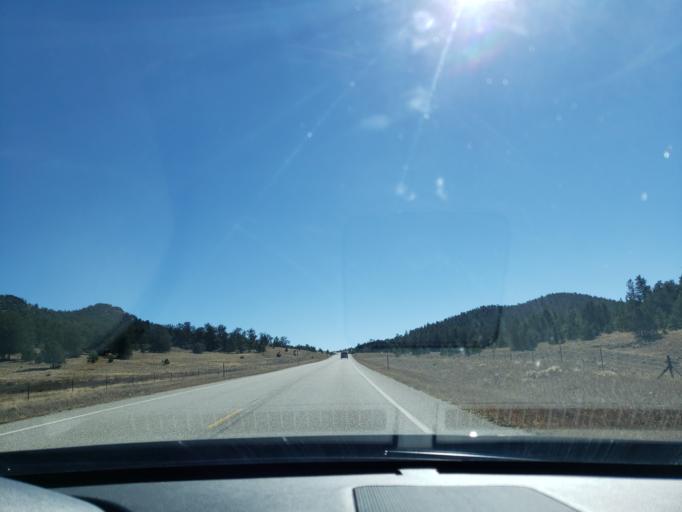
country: US
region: Colorado
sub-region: Chaffee County
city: Salida
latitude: 38.8460
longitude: -105.6442
